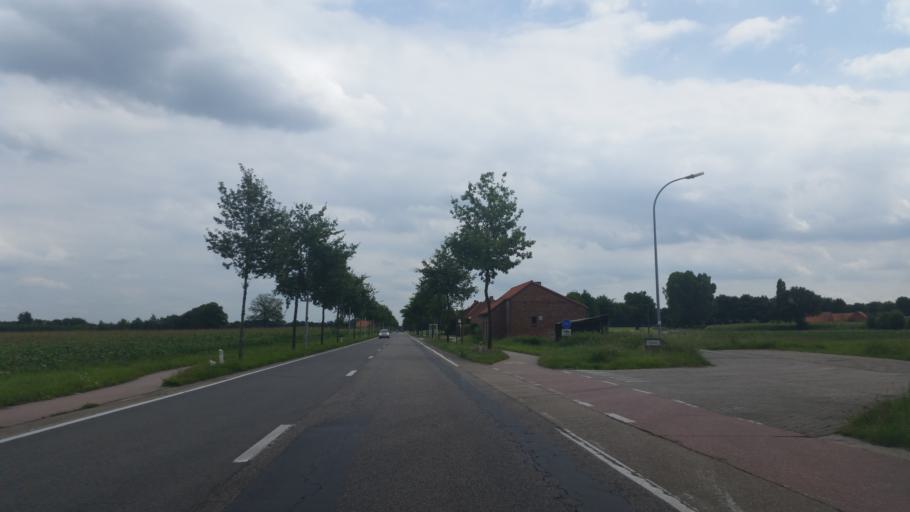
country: BE
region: Flanders
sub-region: Provincie Antwerpen
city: Merksplas
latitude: 51.3453
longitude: 4.8877
